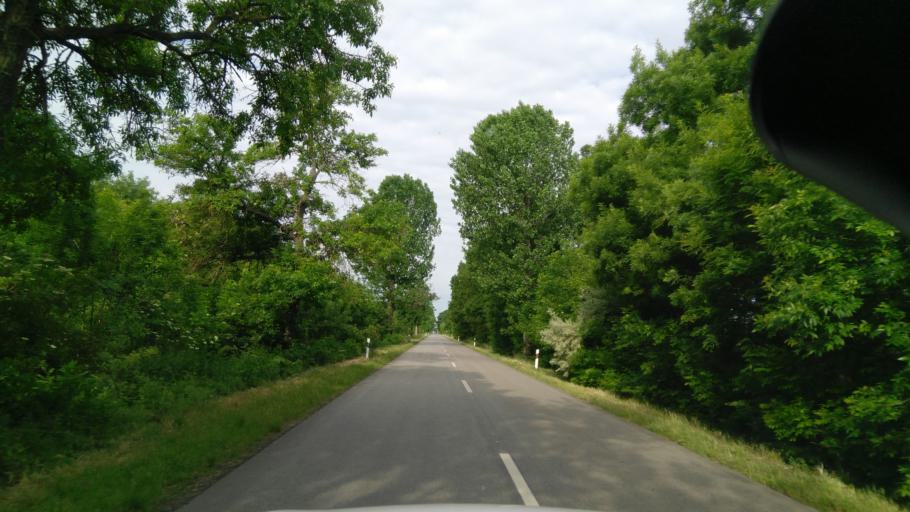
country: HU
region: Bekes
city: Ketegyhaza
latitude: 46.5371
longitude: 21.1371
